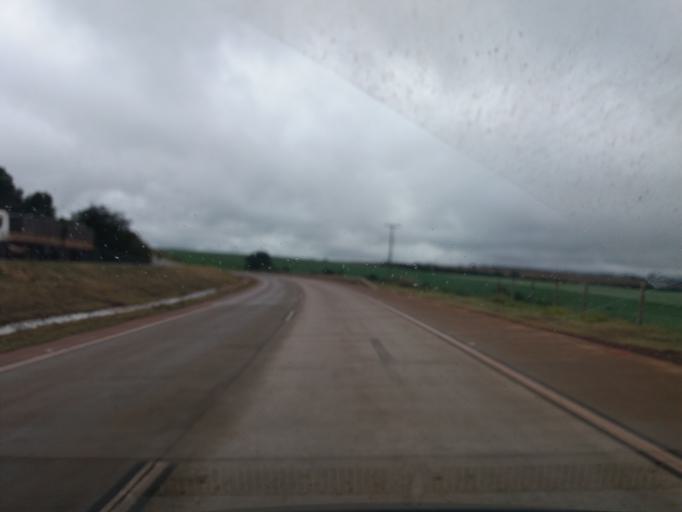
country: BR
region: Parana
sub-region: Cascavel
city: Cascavel
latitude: -25.0475
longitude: -53.5565
